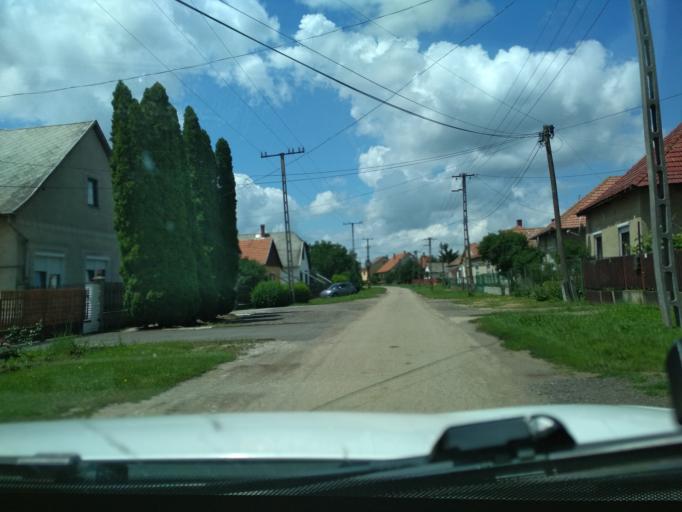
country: HU
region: Jasz-Nagykun-Szolnok
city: Tiszafured
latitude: 47.6107
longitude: 20.7803
